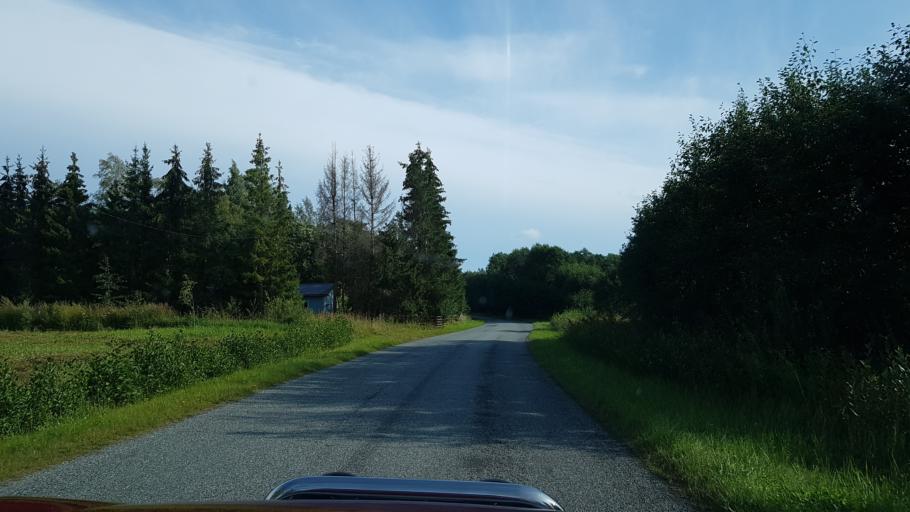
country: EE
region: Laeaene
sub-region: Lihula vald
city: Lihula
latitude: 58.4140
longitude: 24.0139
